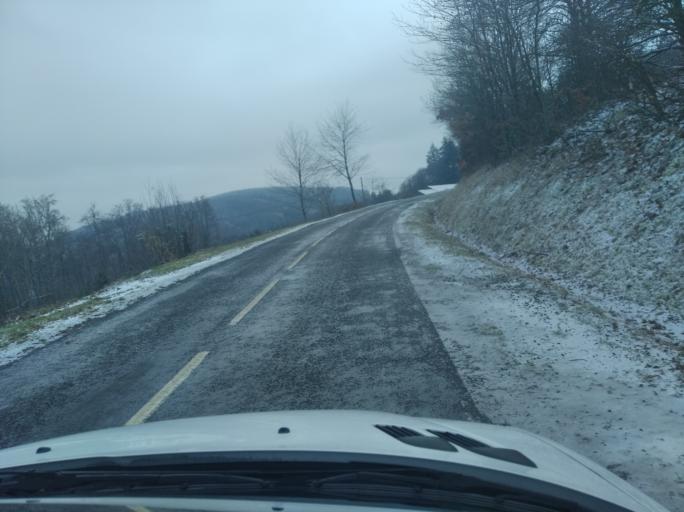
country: FR
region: Rhone-Alpes
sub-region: Departement de la Loire
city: La Pacaudiere
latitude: 46.1301
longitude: 3.7804
